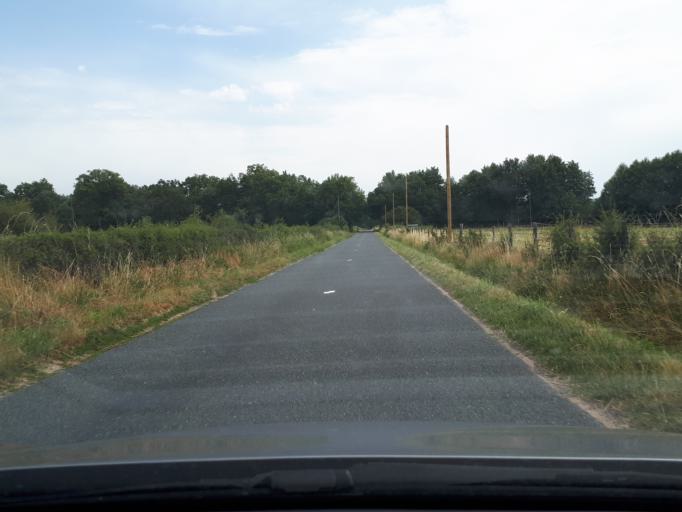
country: FR
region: Rhone-Alpes
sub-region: Departement de la Loire
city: Feurs
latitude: 45.7517
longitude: 4.2346
